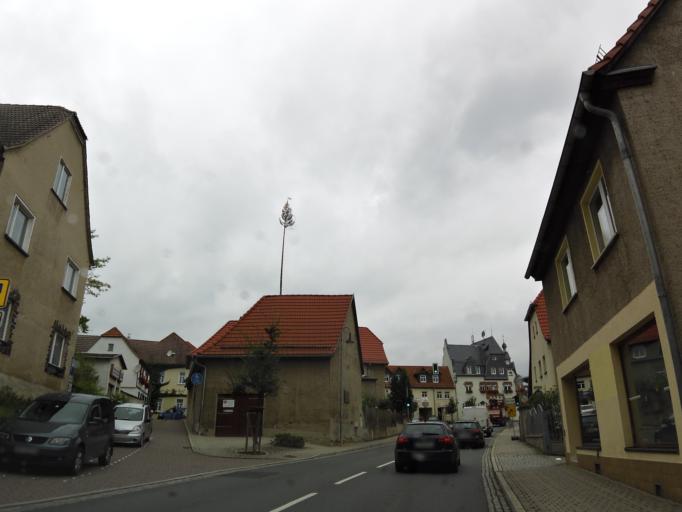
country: DE
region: Thuringia
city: Bad Klosterlausnitz
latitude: 50.9159
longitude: 11.8675
